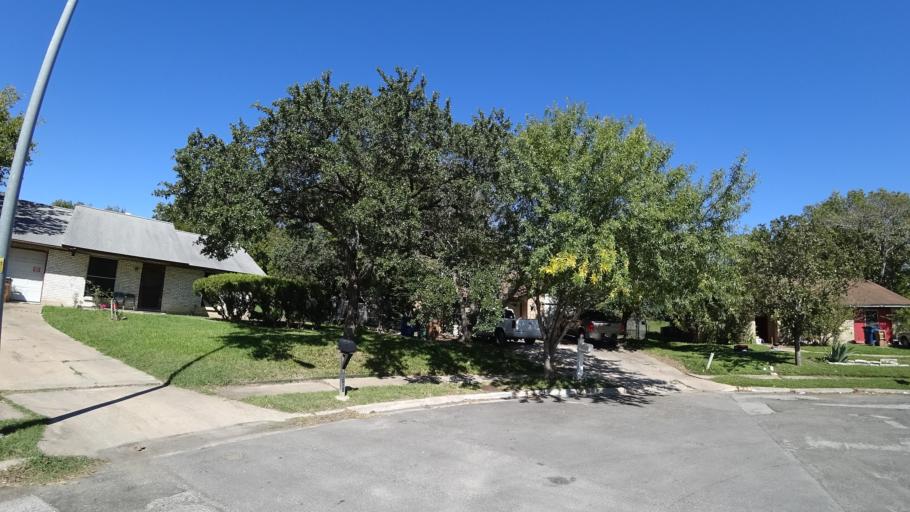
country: US
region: Texas
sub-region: Travis County
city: Hornsby Bend
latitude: 30.3002
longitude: -97.6453
